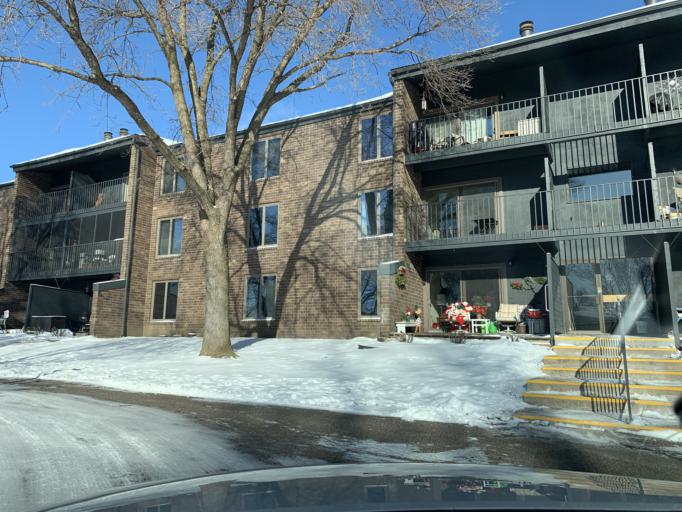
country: US
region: Minnesota
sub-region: Scott County
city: Savage
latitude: 44.8203
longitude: -93.3458
